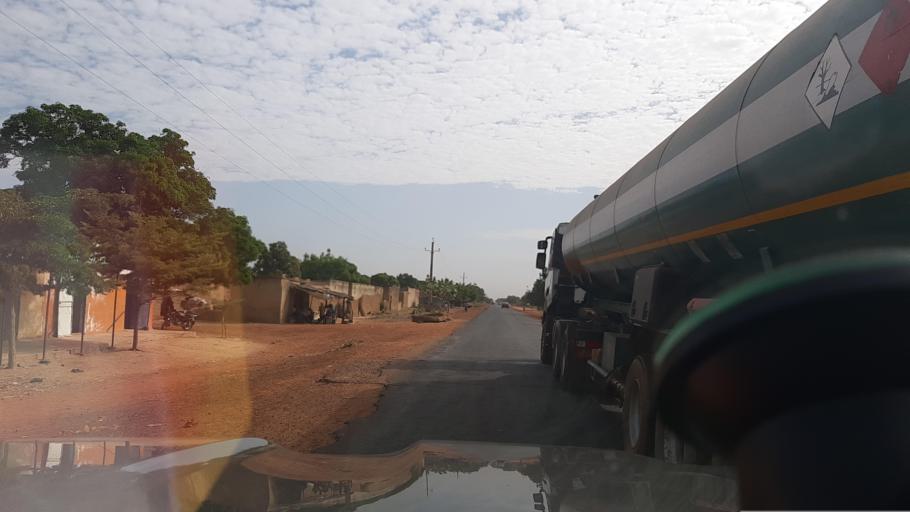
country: ML
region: Segou
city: Segou
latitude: 13.4956
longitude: -6.1693
